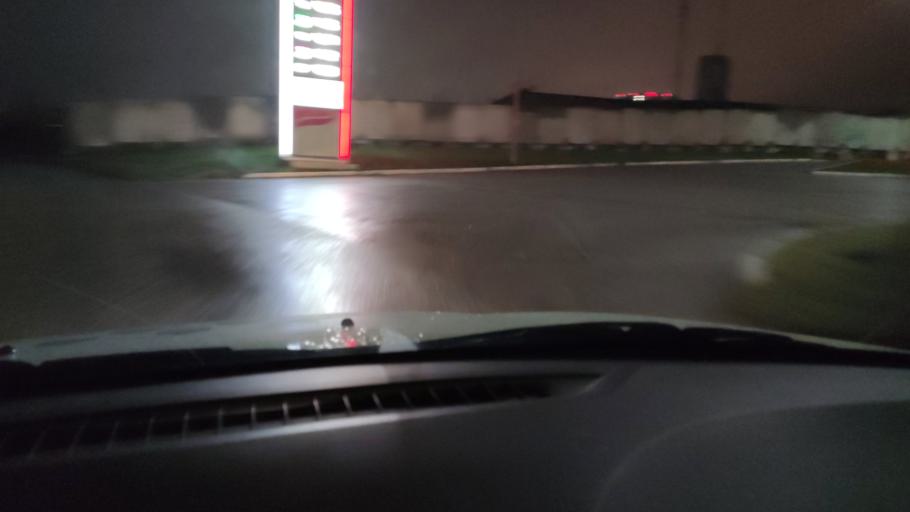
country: RU
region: Perm
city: Kondratovo
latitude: 58.0015
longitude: 56.1371
